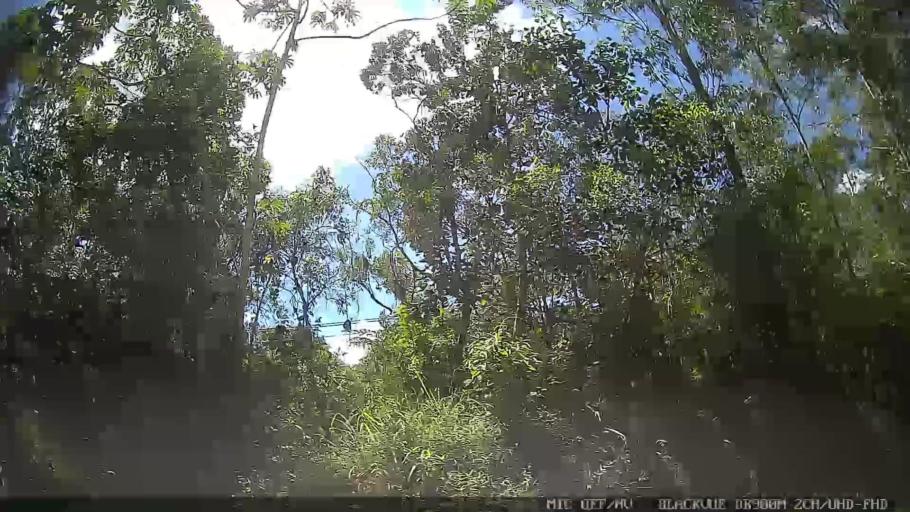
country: BR
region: Sao Paulo
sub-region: Mogi das Cruzes
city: Mogi das Cruzes
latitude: -23.6668
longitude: -46.2092
